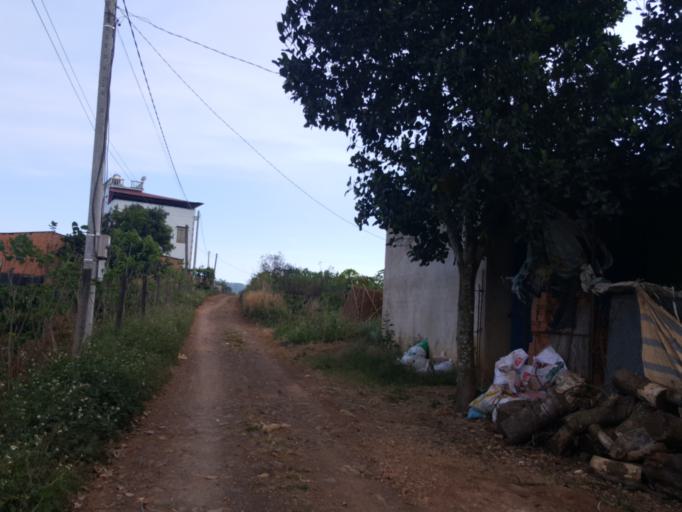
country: VN
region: Lam Dong
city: Duc Trong
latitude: 11.8385
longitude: 108.3478
